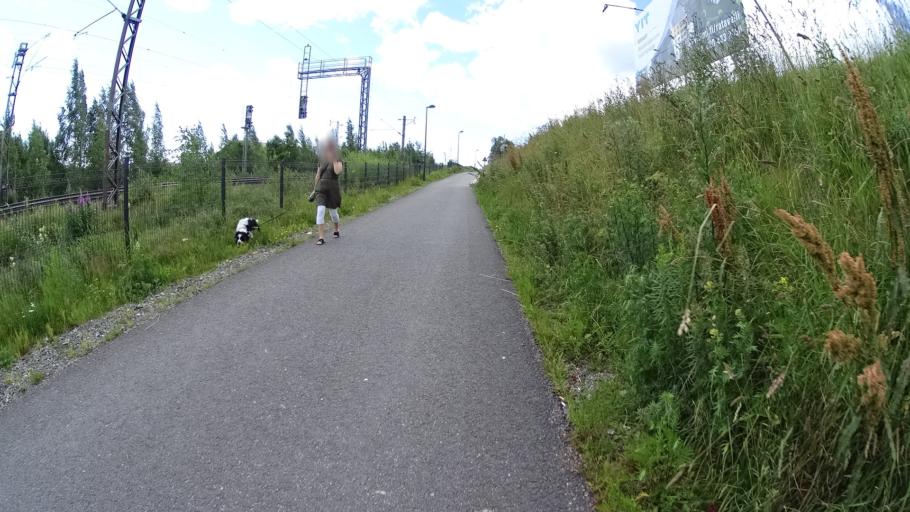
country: FI
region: Uusimaa
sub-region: Helsinki
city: Kirkkonummi
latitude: 60.1560
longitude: 24.5367
